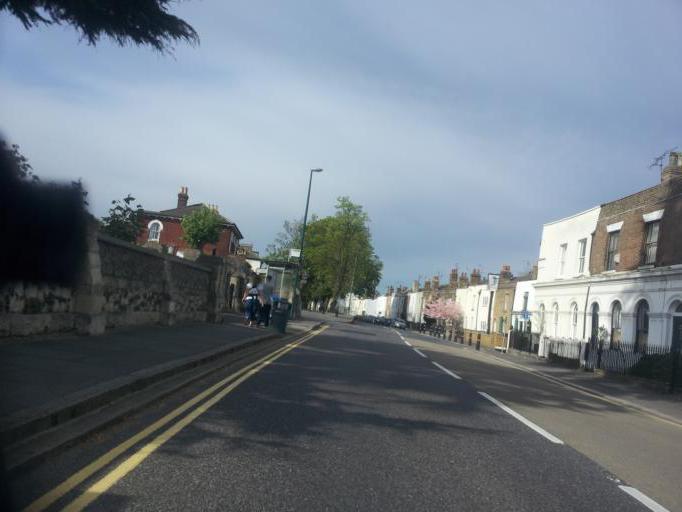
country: GB
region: England
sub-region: Medway
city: Rochester
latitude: 51.3826
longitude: 0.5022
